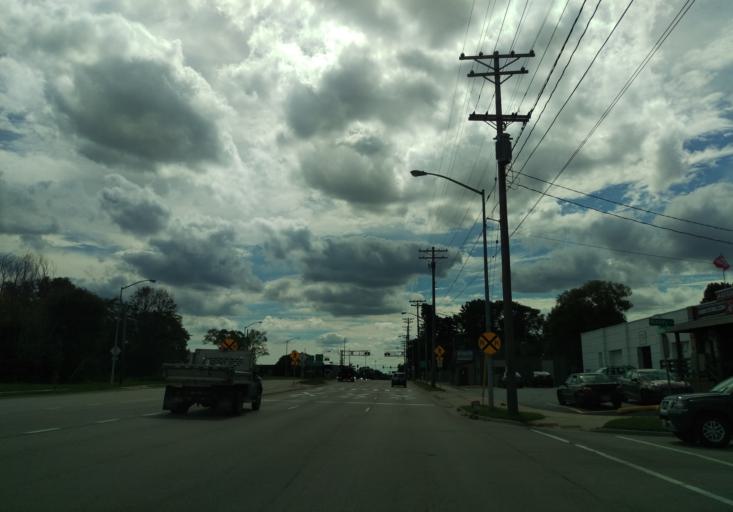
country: US
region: Wisconsin
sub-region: Dane County
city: Maple Bluff
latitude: 43.1241
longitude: -89.3552
